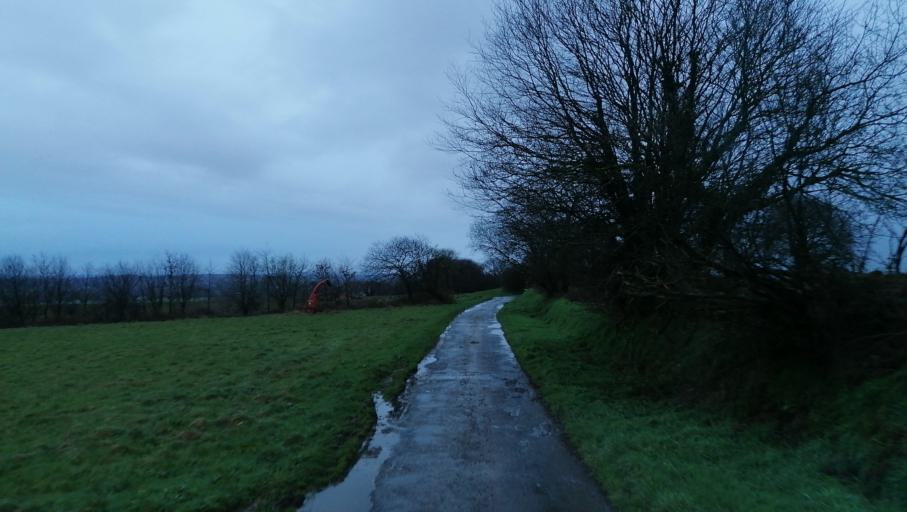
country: FR
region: Brittany
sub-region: Departement des Cotes-d'Armor
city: Plouagat
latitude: 48.4834
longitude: -2.9876
